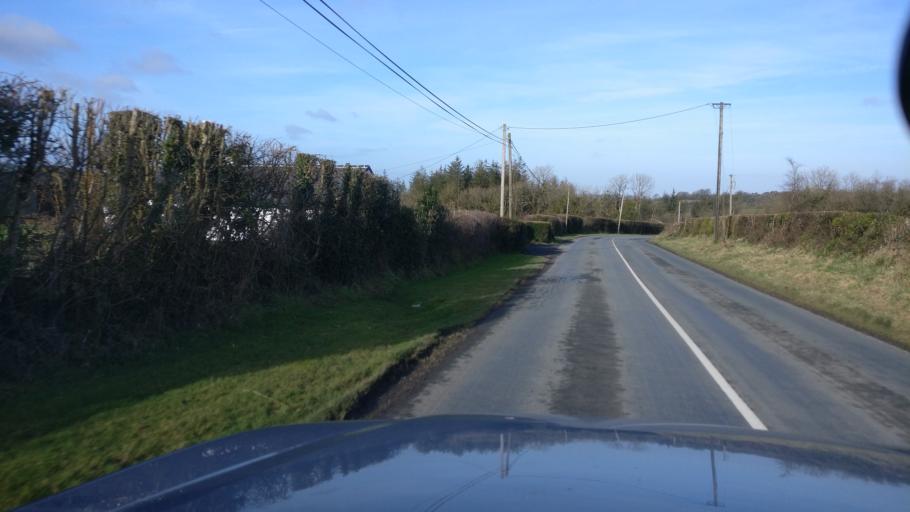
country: IE
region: Leinster
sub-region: Laois
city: Stradbally
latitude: 52.9326
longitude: -7.1981
